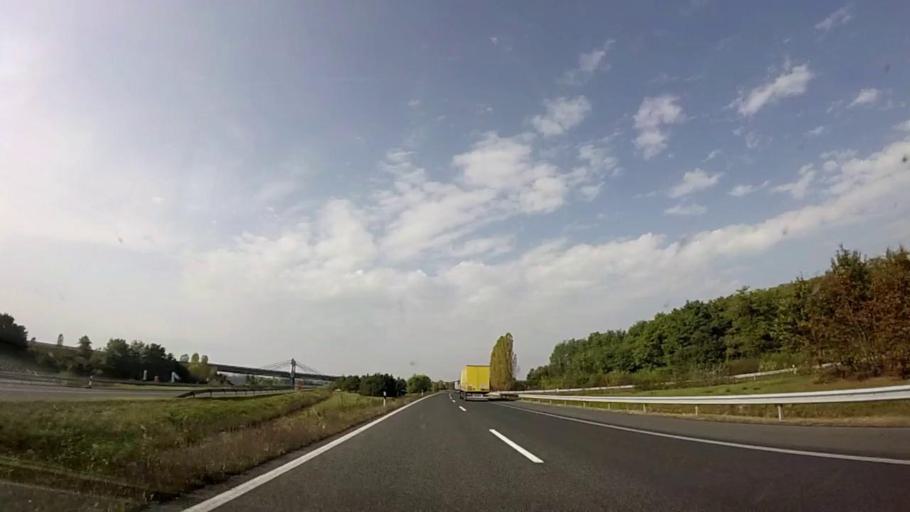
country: HU
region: Zala
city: Letenye
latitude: 46.4144
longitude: 16.7330
